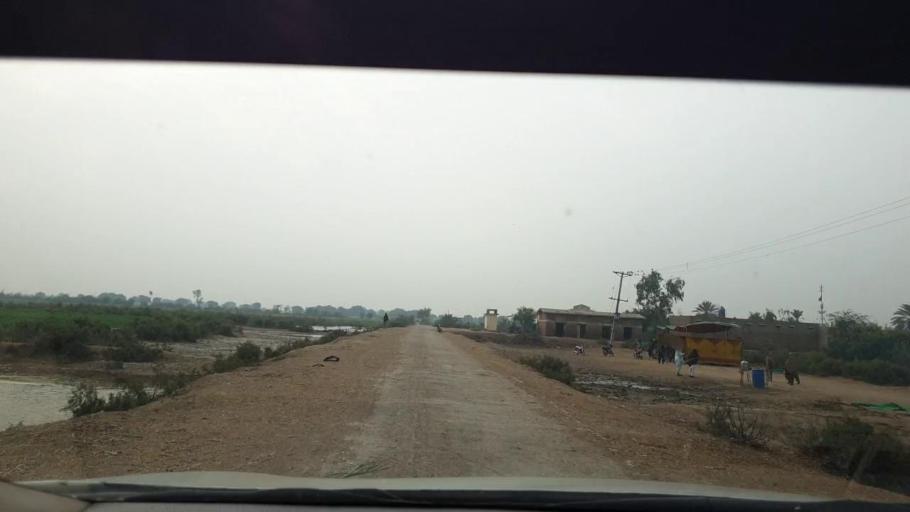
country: PK
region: Sindh
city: Berani
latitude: 25.8601
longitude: 68.8366
